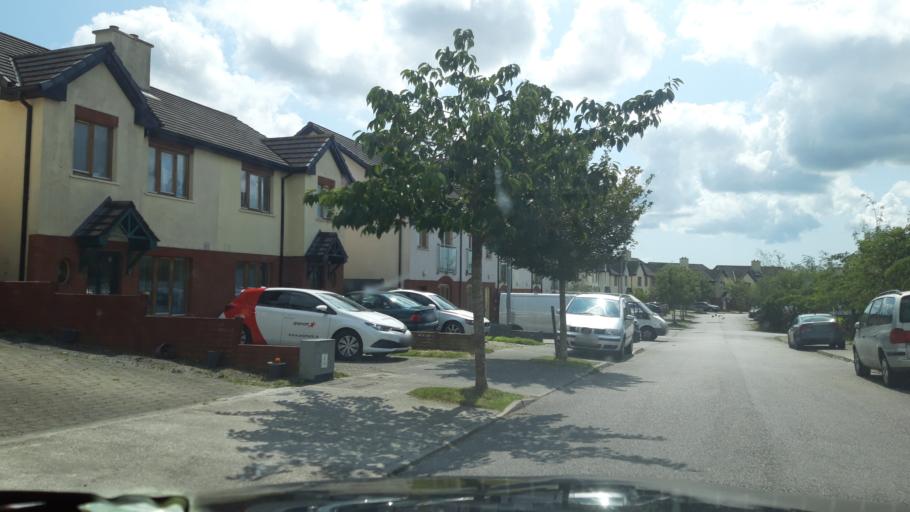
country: IE
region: Munster
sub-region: Waterford
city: Waterford
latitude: 52.2707
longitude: -7.0859
